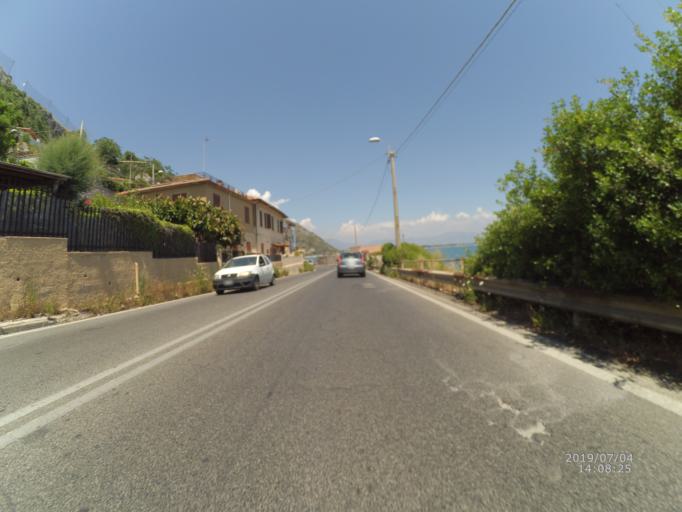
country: IT
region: Latium
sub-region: Provincia di Latina
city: Terracina
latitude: 41.2896
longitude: 13.2636
